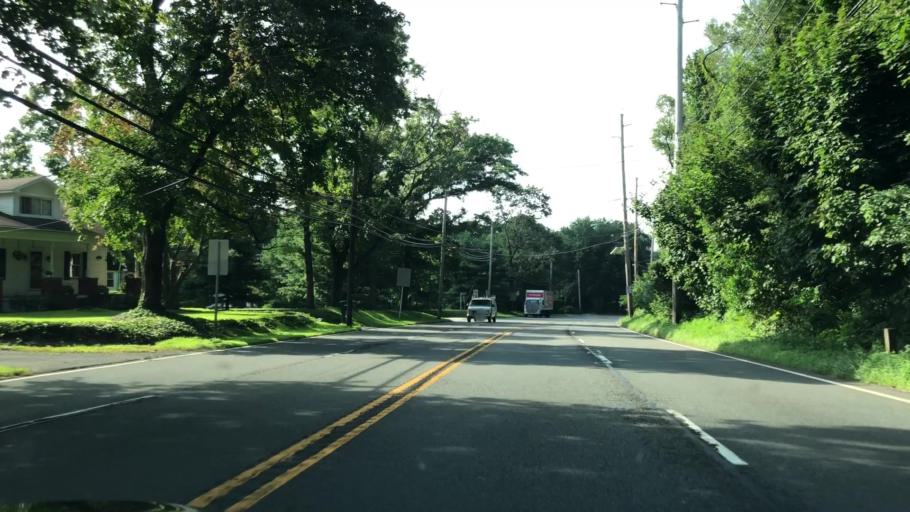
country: US
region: New Jersey
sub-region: Mercer County
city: Ewing
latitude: 40.2972
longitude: -74.7829
